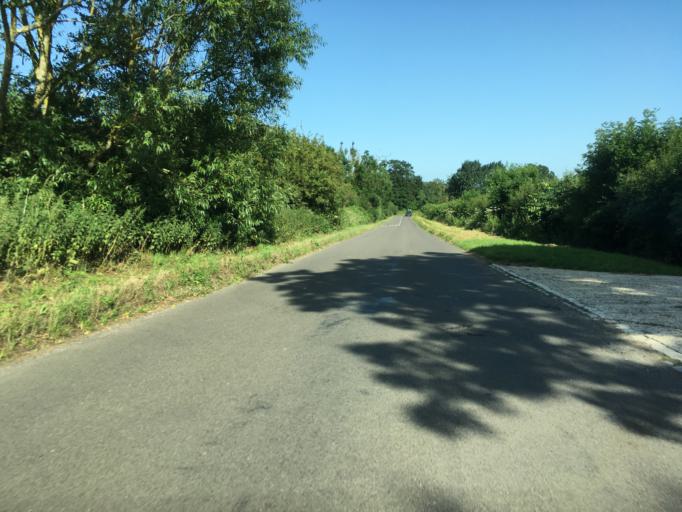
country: GB
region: England
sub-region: Buckinghamshire
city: Steeple Claydon
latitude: 51.9445
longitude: -0.9494
